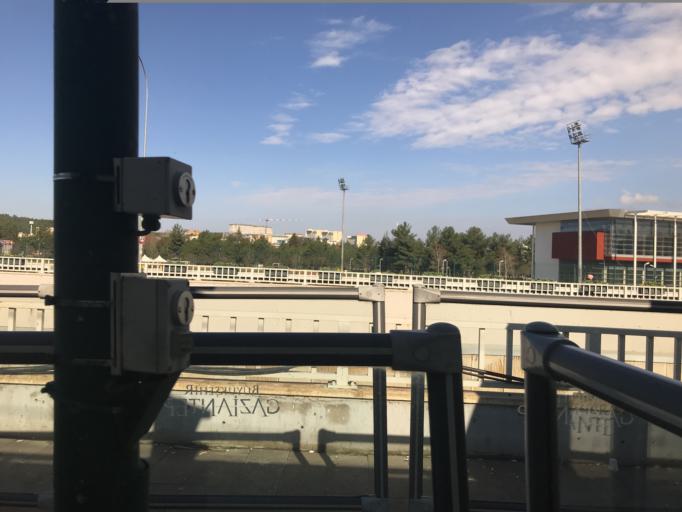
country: TR
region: Gaziantep
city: Sahinbey
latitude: 37.0355
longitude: 37.3184
